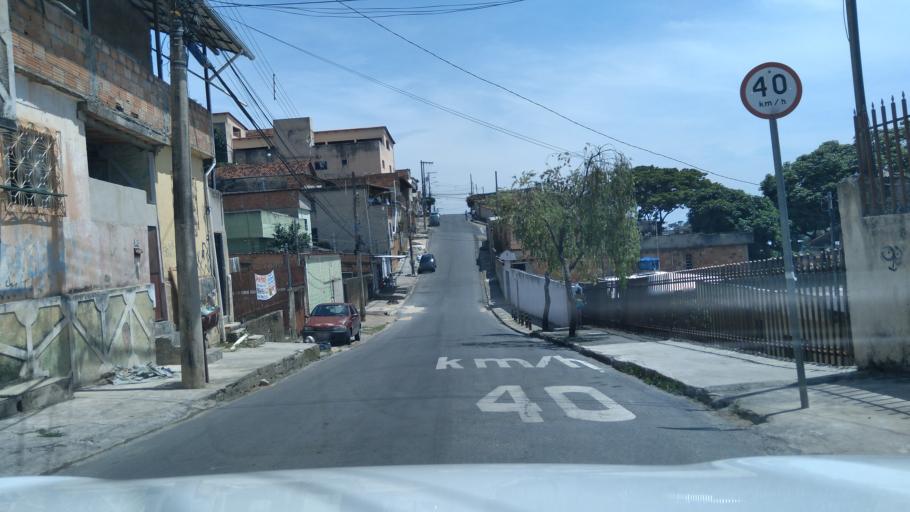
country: BR
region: Minas Gerais
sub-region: Contagem
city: Contagem
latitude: -19.9149
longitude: -44.0242
